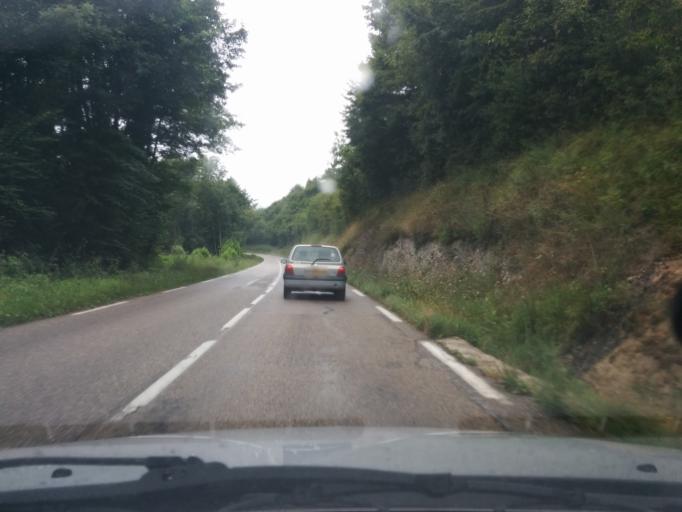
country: FR
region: Rhone-Alpes
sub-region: Departement de l'Isere
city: Saint-Geoire-en-Valdaine
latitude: 45.4722
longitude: 5.6666
